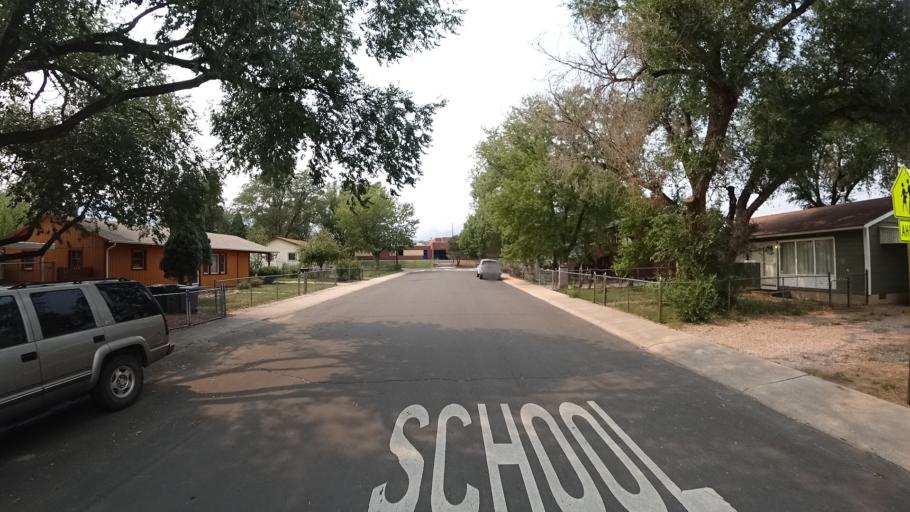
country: US
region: Colorado
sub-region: El Paso County
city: Stratmoor
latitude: 38.7983
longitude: -104.8080
